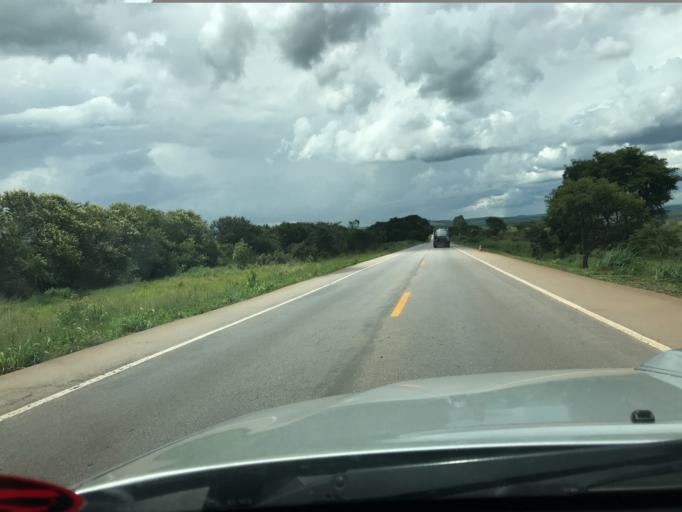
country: BR
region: Minas Gerais
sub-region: Ibia
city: Ibia
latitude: -19.5840
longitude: -46.4587
